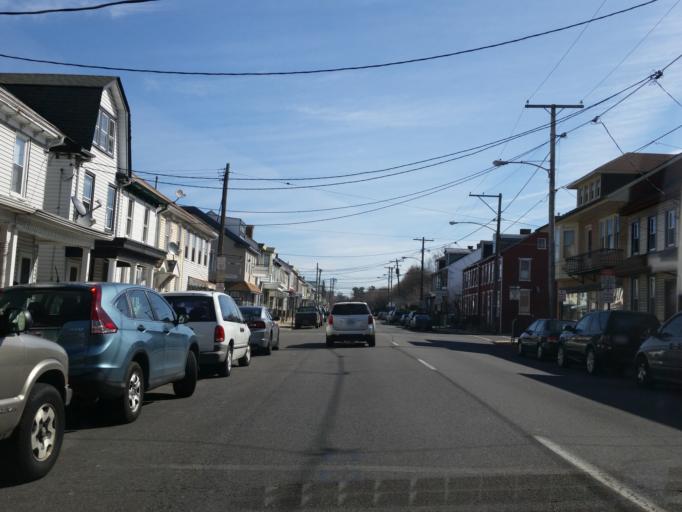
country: US
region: Pennsylvania
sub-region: Lebanon County
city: Lebanon
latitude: 40.3370
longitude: -76.4198
